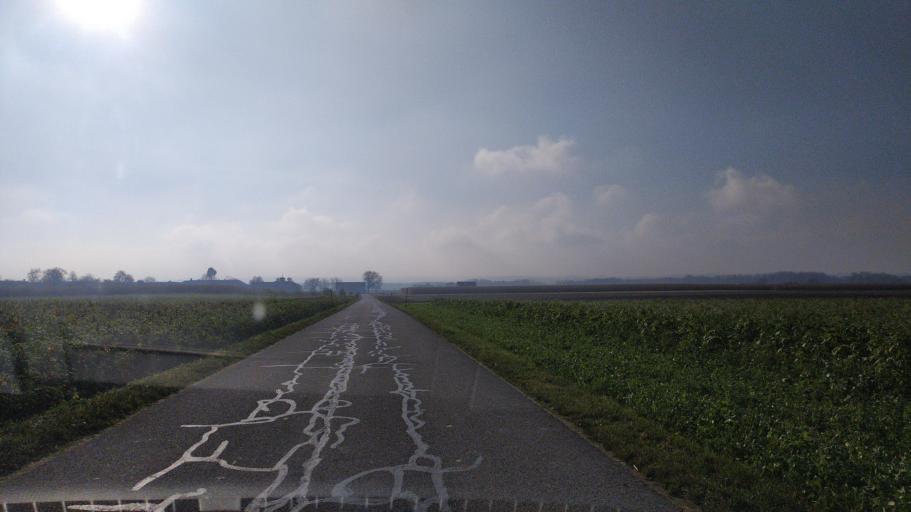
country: AT
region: Upper Austria
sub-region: Politischer Bezirk Perg
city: Perg
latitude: 48.2004
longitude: 14.6517
